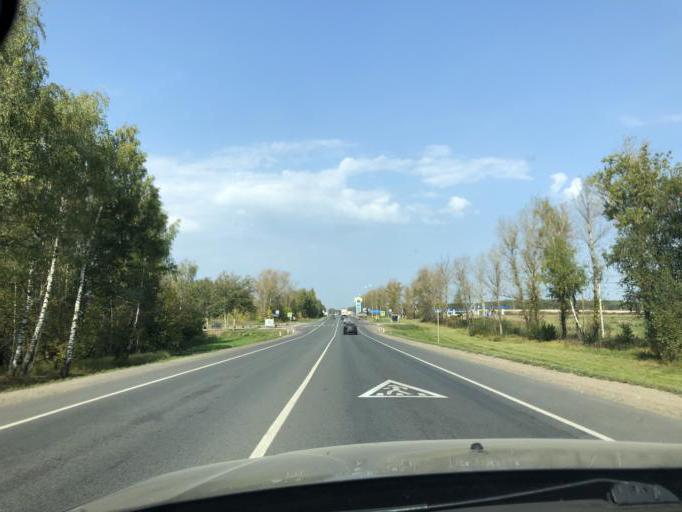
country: RU
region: Moskovskaya
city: L'vovskiy
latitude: 55.3420
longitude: 37.4608
